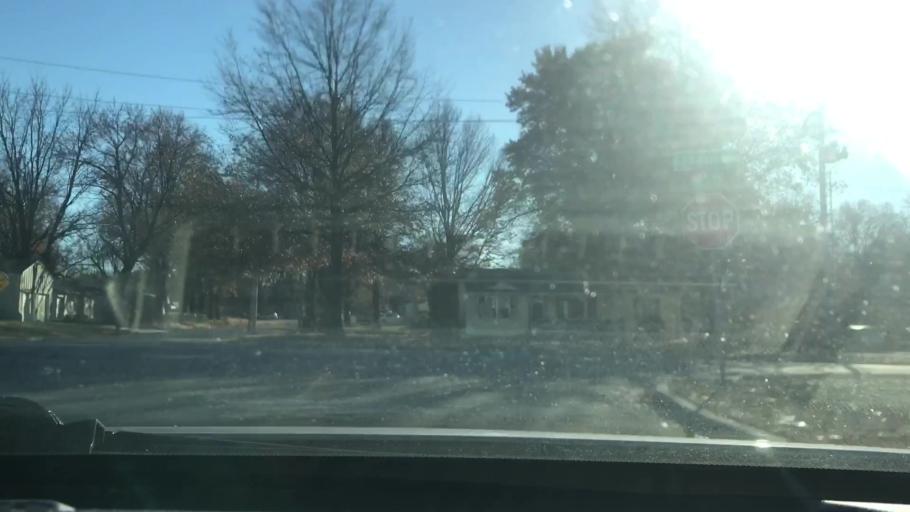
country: US
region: Missouri
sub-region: Jackson County
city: Grandview
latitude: 38.9167
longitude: -94.5302
